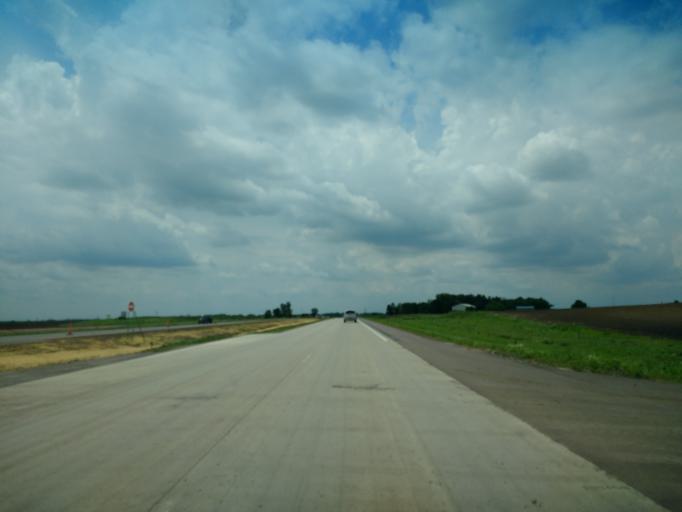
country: US
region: Minnesota
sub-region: Cottonwood County
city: Windom
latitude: 43.8955
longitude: -95.0797
